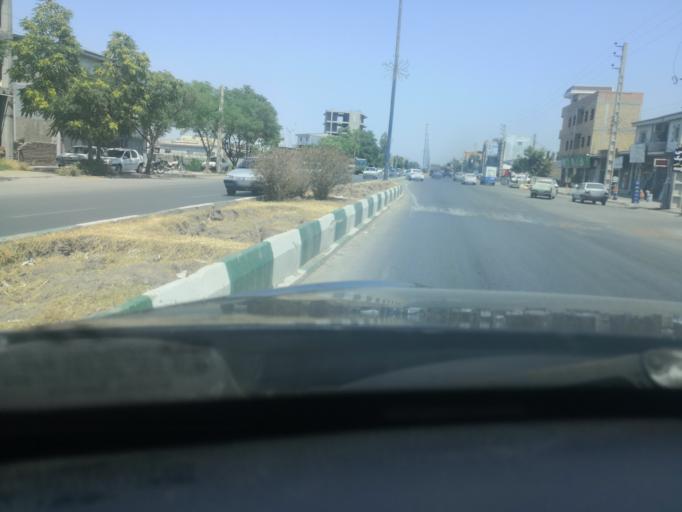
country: IR
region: Golestan
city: Aq Qala
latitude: 37.0091
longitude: 54.4668
